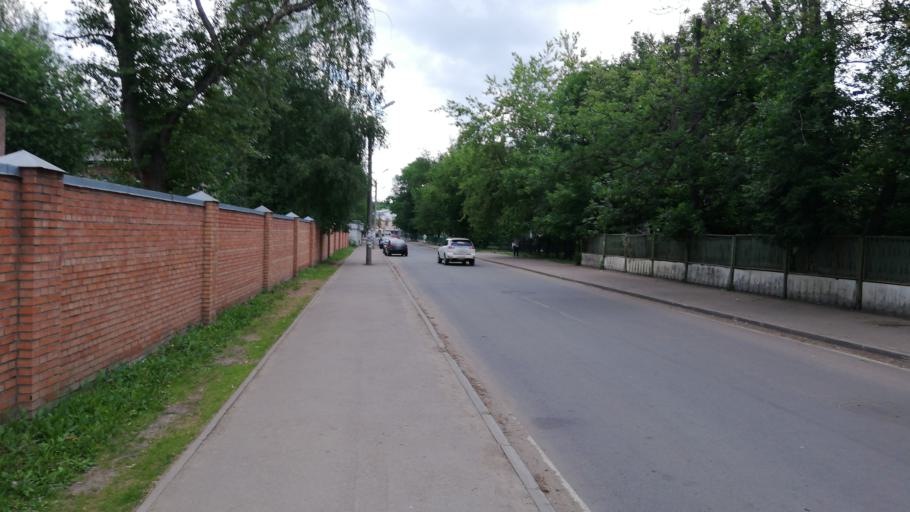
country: RU
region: Jaroslavl
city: Yaroslavl
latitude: 57.6386
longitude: 39.8640
